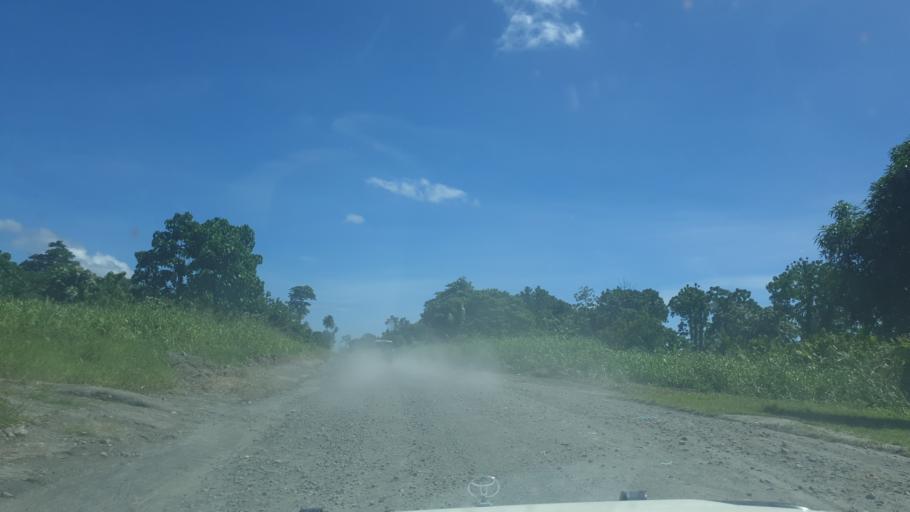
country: PG
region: Bougainville
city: Arawa
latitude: -5.9854
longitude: 155.3569
